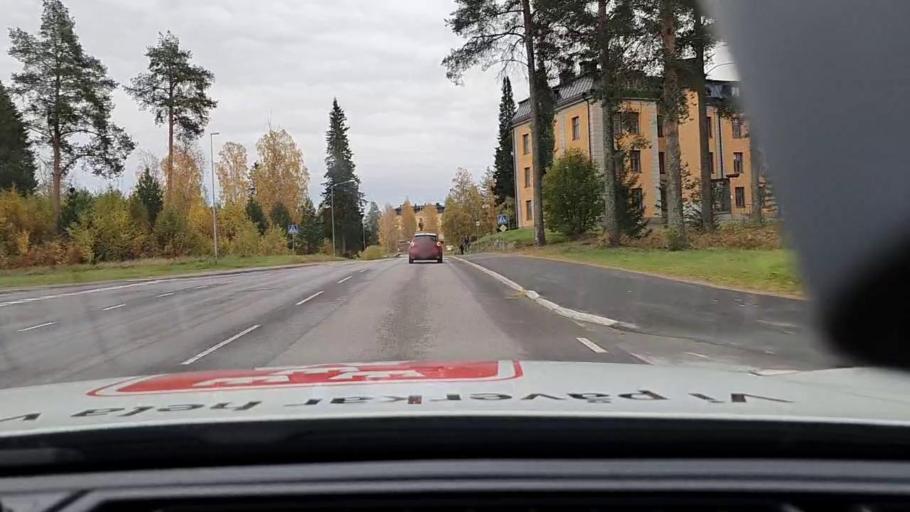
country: SE
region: Norrbotten
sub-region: Bodens Kommun
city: Boden
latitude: 65.8151
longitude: 21.6744
